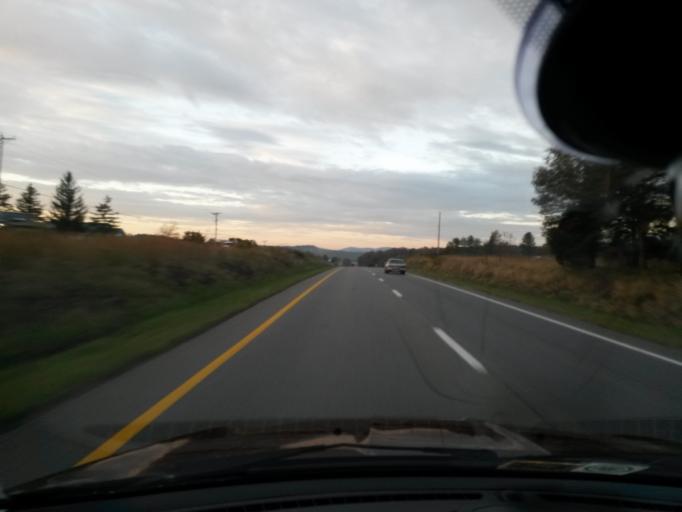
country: US
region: Virginia
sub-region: Botetourt County
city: Fincastle
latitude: 37.5399
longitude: -79.8641
